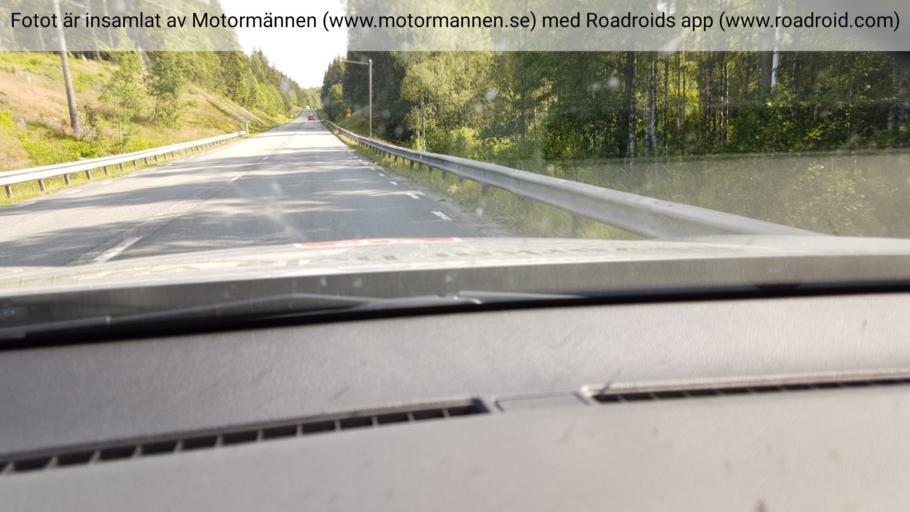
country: SE
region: Joenkoeping
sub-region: Tranas Kommun
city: Tranas
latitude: 57.9621
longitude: 14.9157
